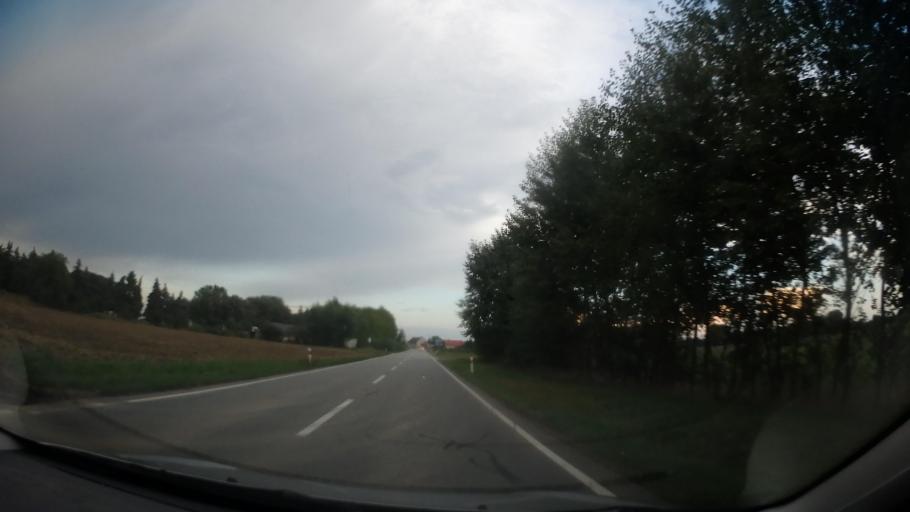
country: CZ
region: Olomoucky
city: Troubky
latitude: 49.4293
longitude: 17.3348
